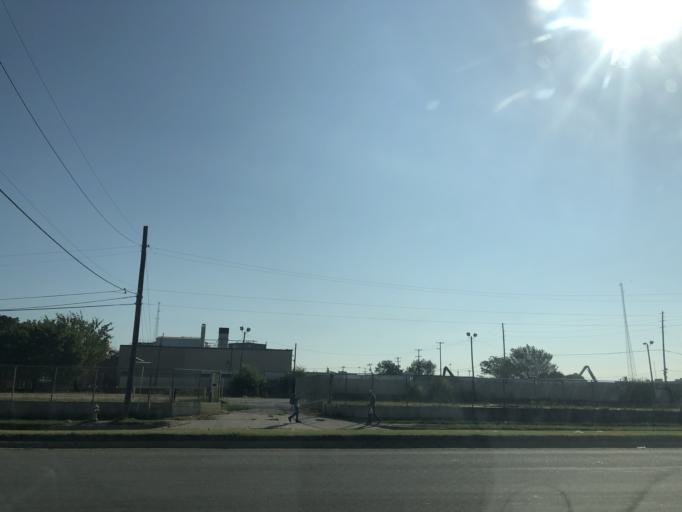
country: US
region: Texas
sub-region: Dallas County
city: Dallas
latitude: 32.7724
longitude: -96.7825
